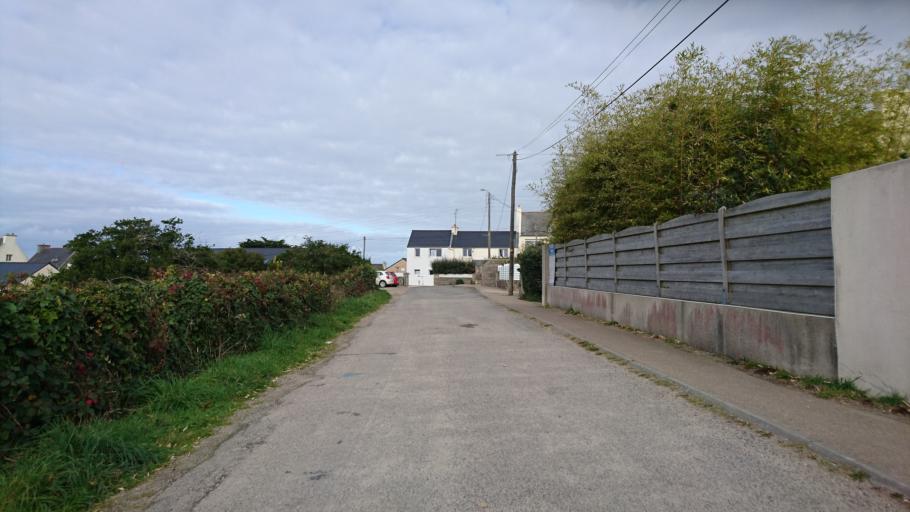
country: FR
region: Brittany
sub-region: Departement du Finistere
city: Lampaul-Plouarzel
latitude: 48.4462
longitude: -4.7618
